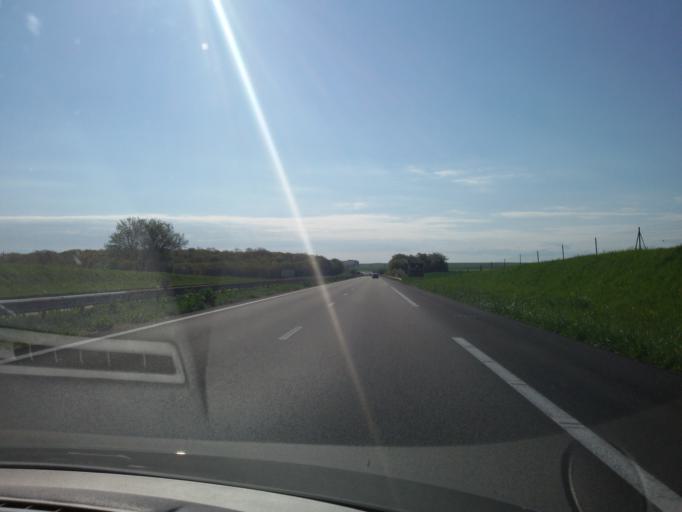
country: FR
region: Bourgogne
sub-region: Departement de l'Yonne
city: Vermenton
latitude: 47.7077
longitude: 3.7933
